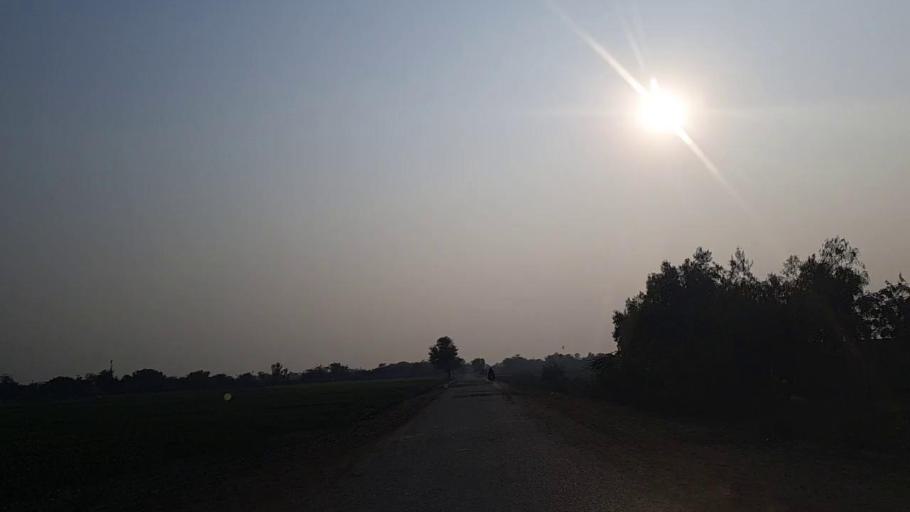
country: PK
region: Sindh
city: Nawabshah
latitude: 26.2207
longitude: 68.4759
